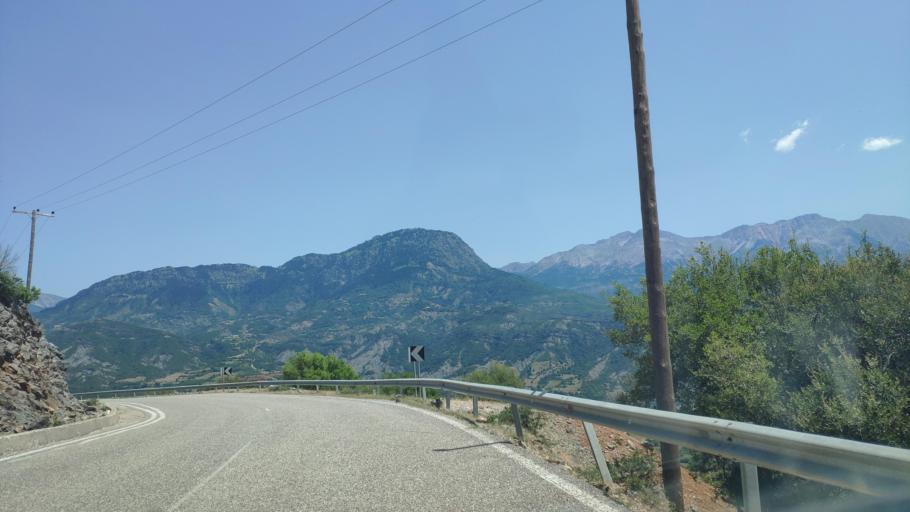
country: GR
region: Central Greece
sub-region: Nomos Evrytanias
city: Kerasochori
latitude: 39.0962
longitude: 21.4123
